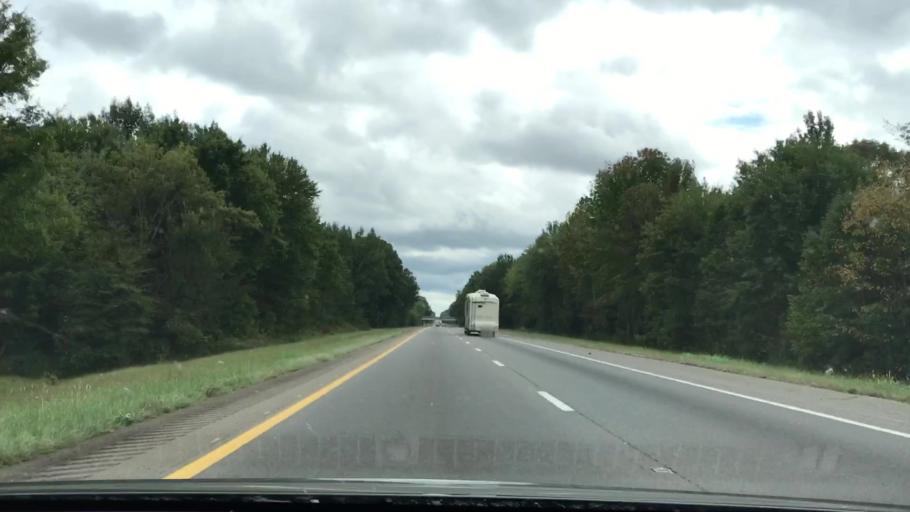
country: US
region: Tennessee
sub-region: Cheatham County
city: Pleasant View
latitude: 36.4364
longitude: -87.0791
